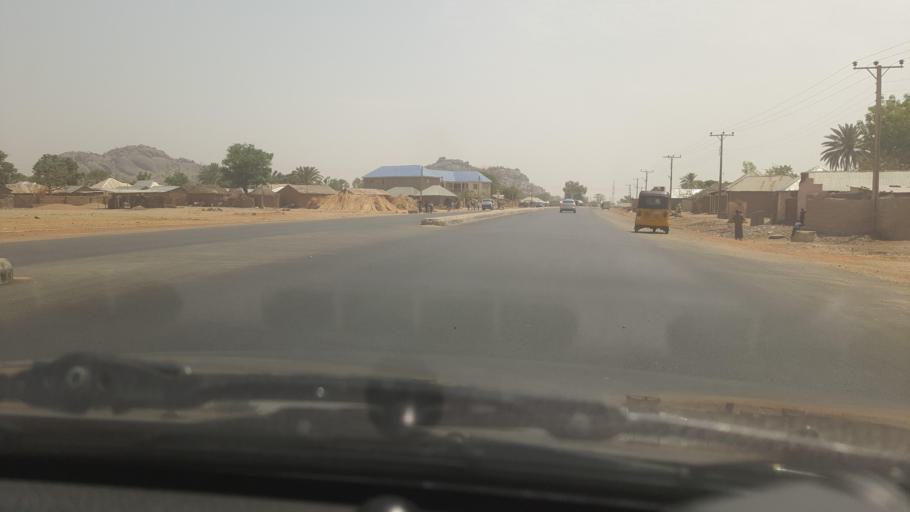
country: NG
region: Bauchi
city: Bauchi
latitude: 10.3022
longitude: 9.7399
